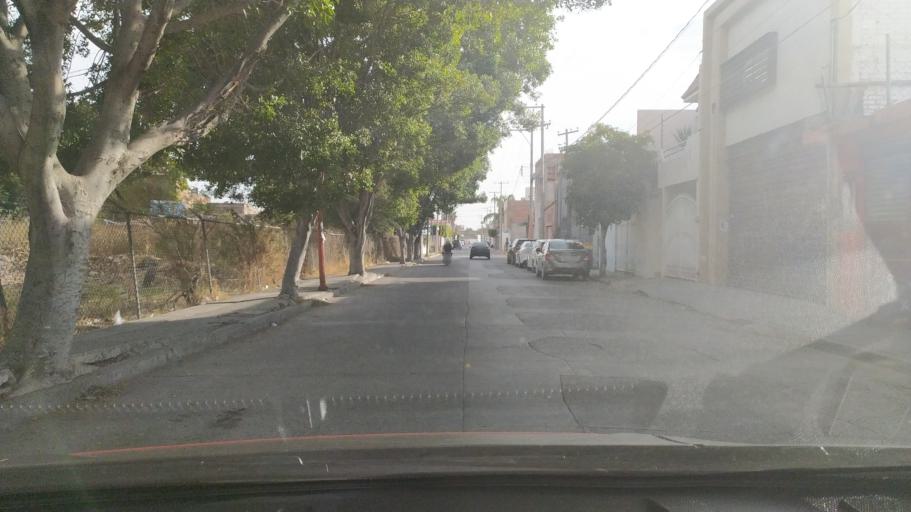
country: MX
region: Guanajuato
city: San Francisco del Rincon
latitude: 21.0281
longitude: -101.8563
